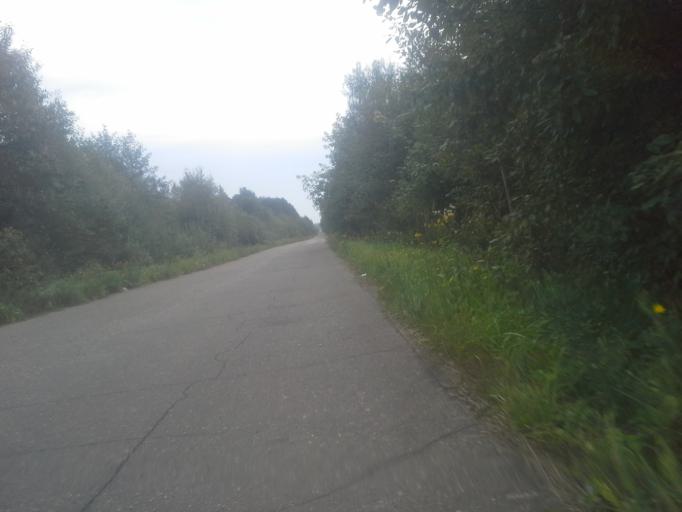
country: RU
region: Moskovskaya
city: Kievskij
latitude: 55.3876
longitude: 36.9033
